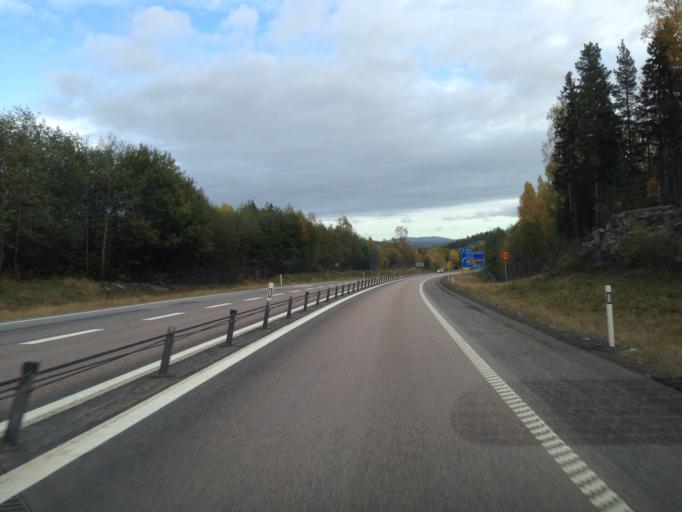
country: SE
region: Vaesternorrland
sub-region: Haernoesands Kommun
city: Haernoesand
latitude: 62.8083
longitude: 17.9537
